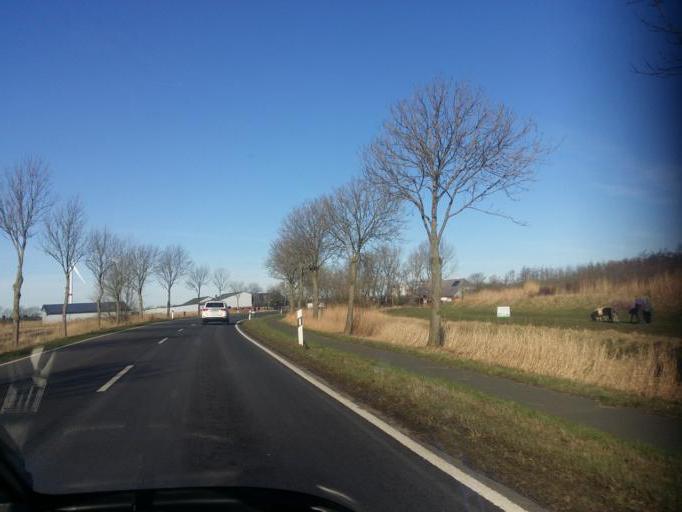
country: DE
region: Schleswig-Holstein
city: Husum
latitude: 54.4542
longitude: 9.0437
